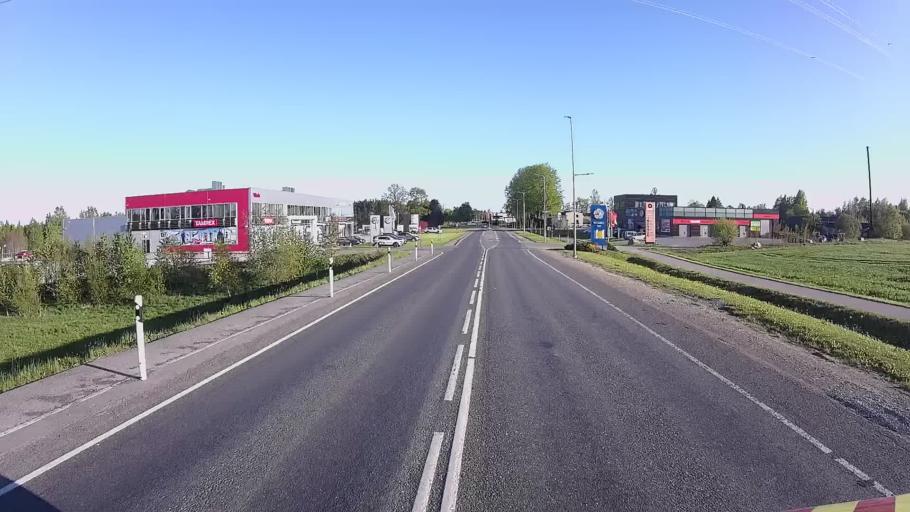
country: EE
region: Viljandimaa
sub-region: Viljandi linn
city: Viljandi
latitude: 58.3831
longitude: 25.5951
